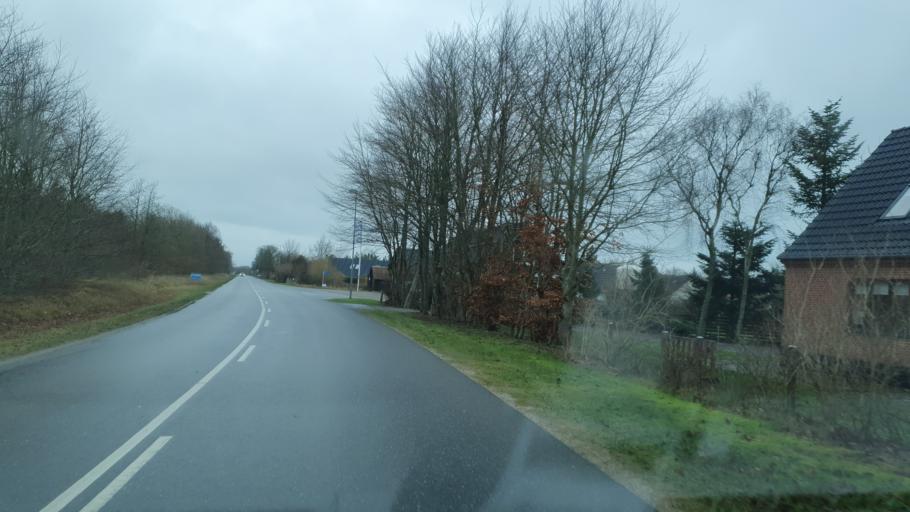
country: DK
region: North Denmark
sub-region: Jammerbugt Kommune
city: Fjerritslev
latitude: 57.1311
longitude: 9.1331
